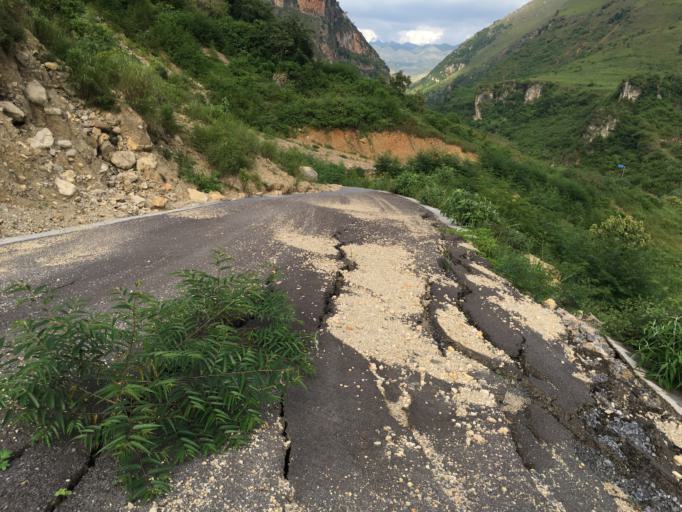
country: CN
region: Guizhou Sheng
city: Anshun
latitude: 25.7778
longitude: 105.3897
